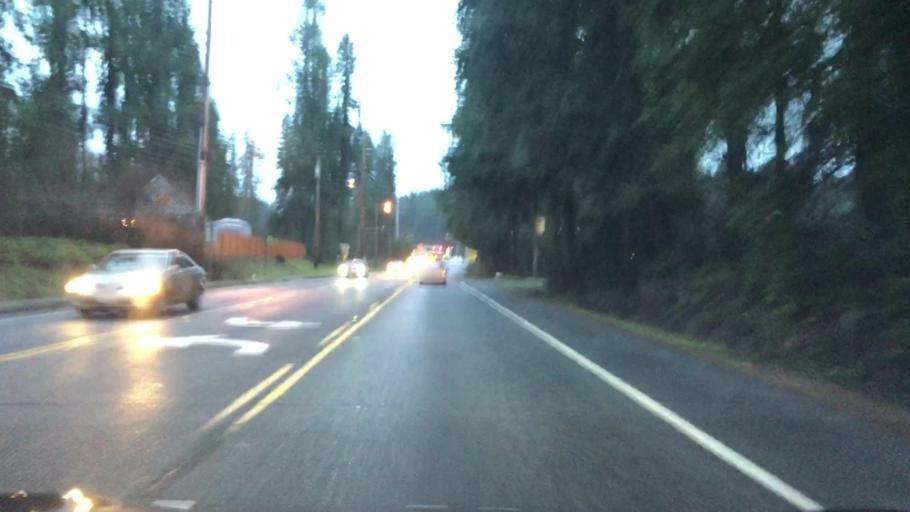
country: US
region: Washington
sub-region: King County
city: Cottage Lake
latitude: 47.7520
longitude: -122.0812
